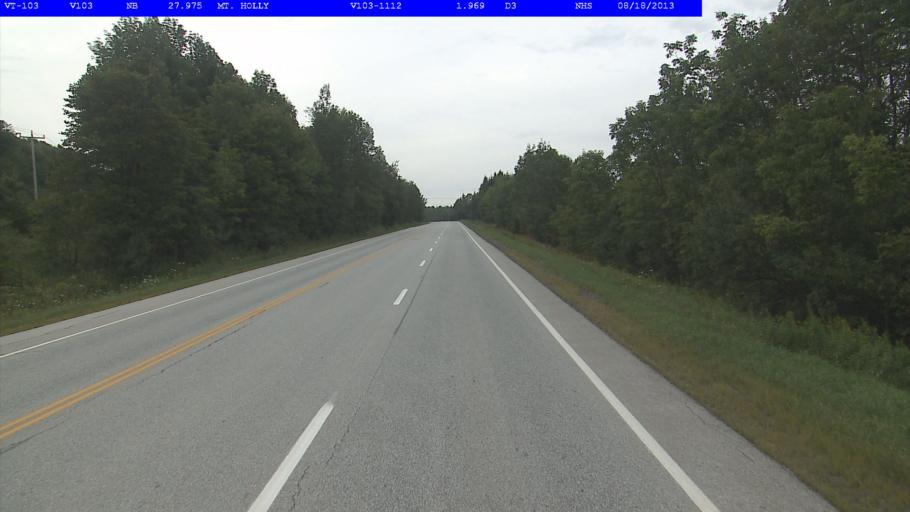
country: US
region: Vermont
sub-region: Windsor County
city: Chester
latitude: 43.4434
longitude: -72.7688
